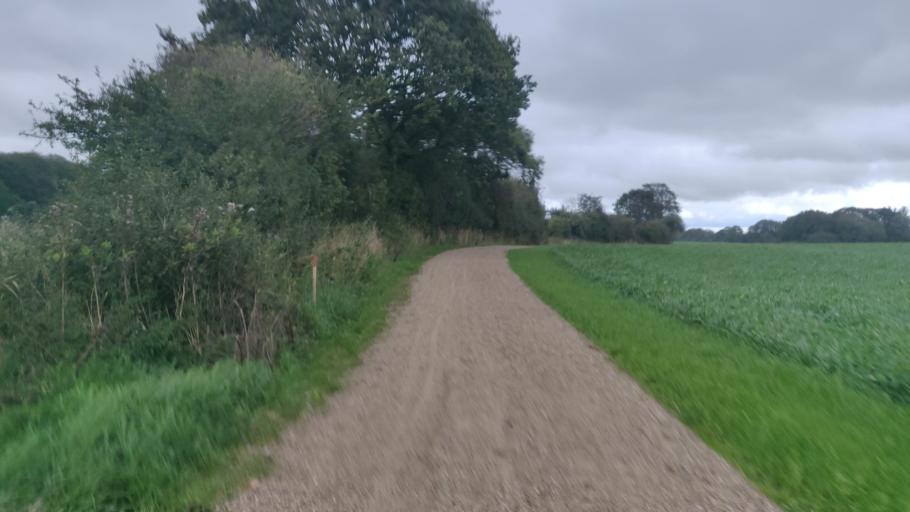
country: DK
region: South Denmark
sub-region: Kolding Kommune
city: Lunderskov
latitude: 55.5382
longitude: 9.3354
